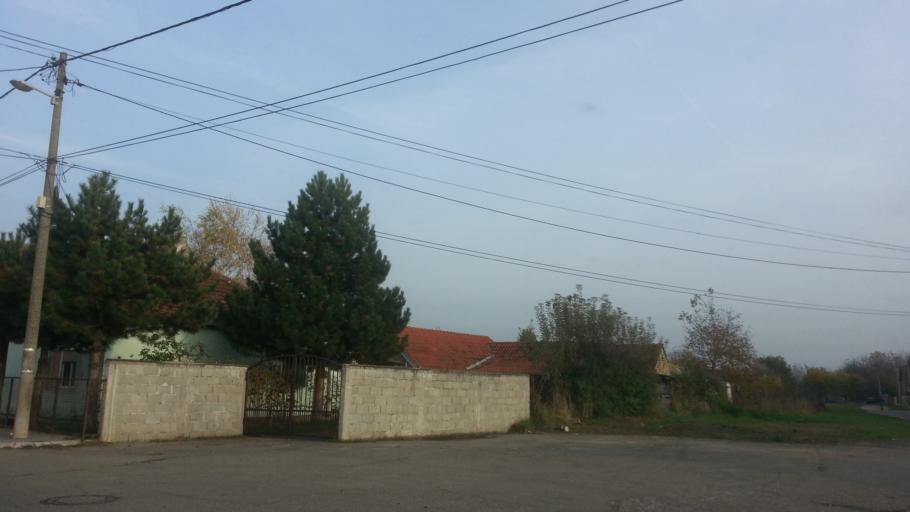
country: RS
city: Novi Banovci
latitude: 44.8928
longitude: 20.2841
